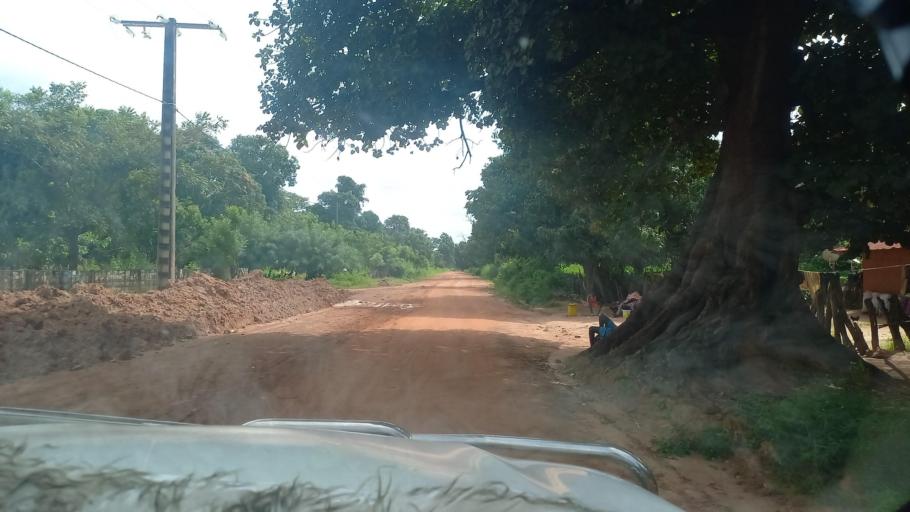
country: SN
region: Ziguinchor
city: Bignona
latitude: 12.7515
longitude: -16.2799
